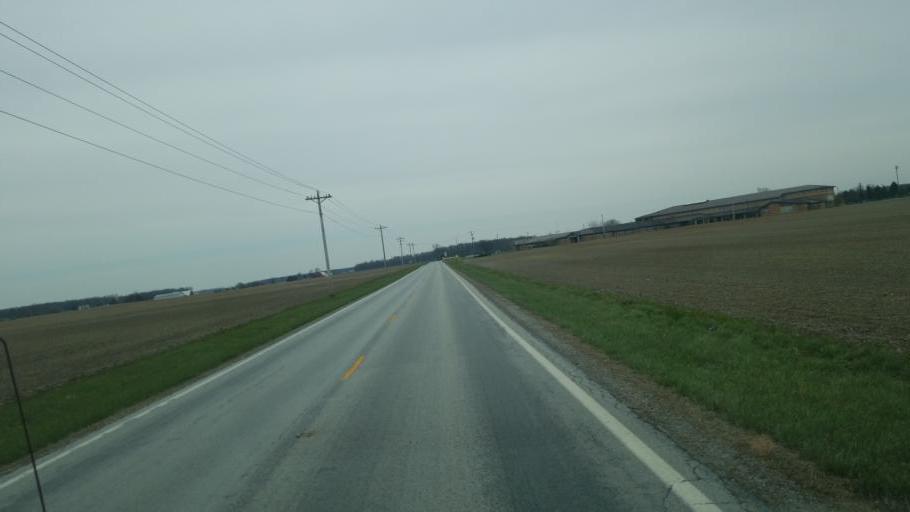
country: US
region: Ohio
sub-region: Hardin County
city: Forest
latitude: 40.8624
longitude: -83.5201
